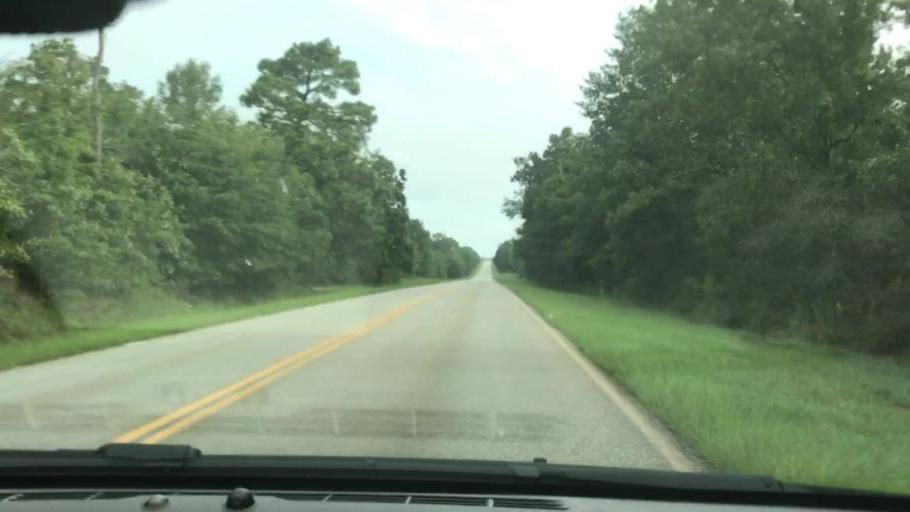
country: US
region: Georgia
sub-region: Stewart County
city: Lumpkin
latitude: 31.9997
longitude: -84.9325
